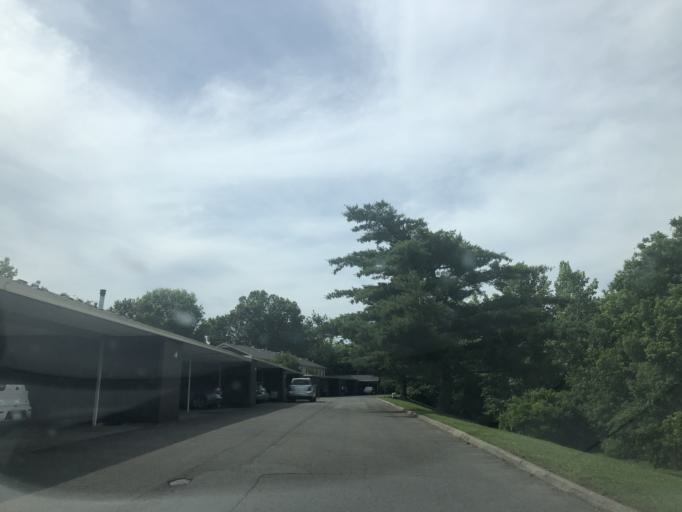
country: US
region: Tennessee
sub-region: Davidson County
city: Belle Meade
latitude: 36.0734
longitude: -86.9501
